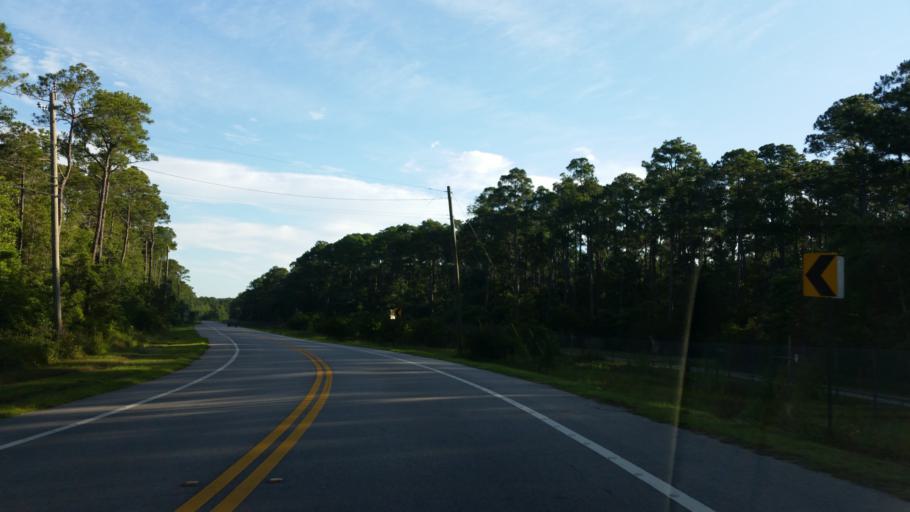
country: US
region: Florida
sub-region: Escambia County
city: Warrington
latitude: 30.3439
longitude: -87.3424
